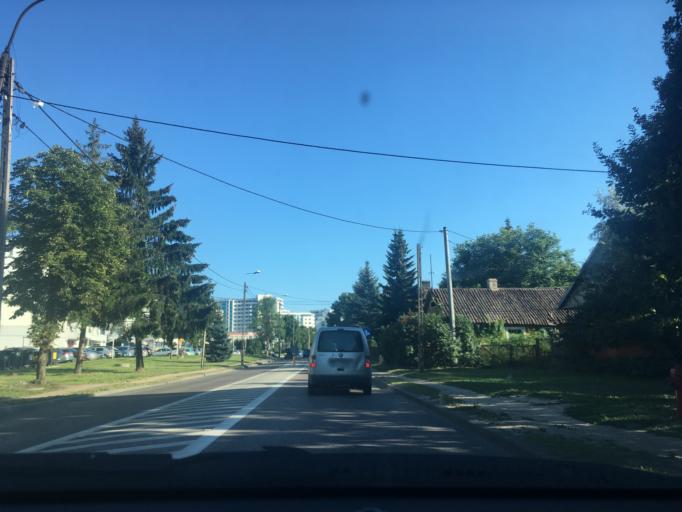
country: PL
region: Podlasie
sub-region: Bialystok
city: Bialystok
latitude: 53.1559
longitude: 23.1519
